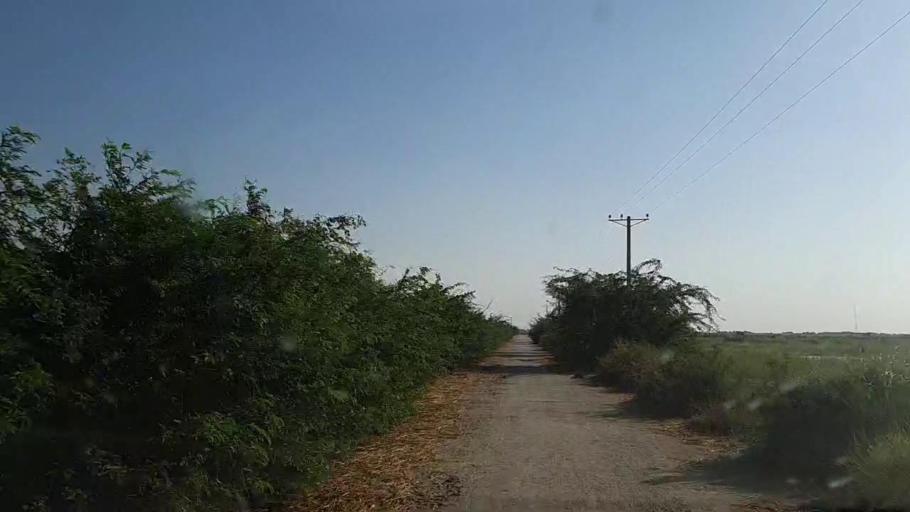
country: PK
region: Sindh
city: Thatta
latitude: 24.6439
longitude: 68.0752
